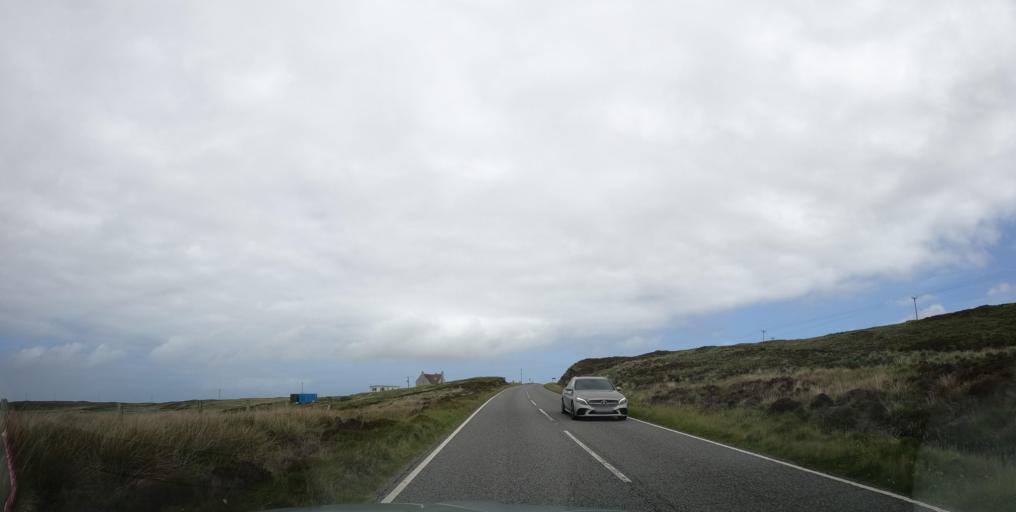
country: GB
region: Scotland
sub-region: Eilean Siar
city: Isle of South Uist
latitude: 57.2683
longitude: -7.3682
